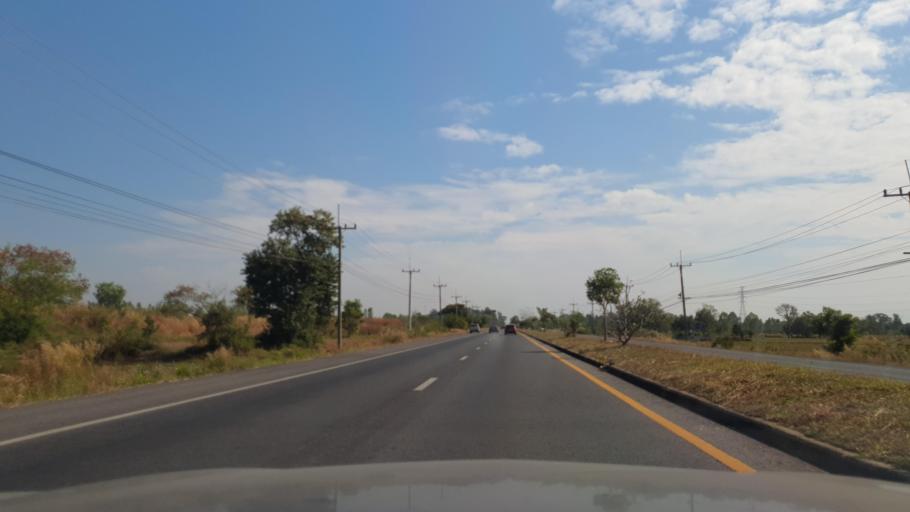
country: TH
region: Maha Sarakham
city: Kantharawichai
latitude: 16.3849
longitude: 103.2331
